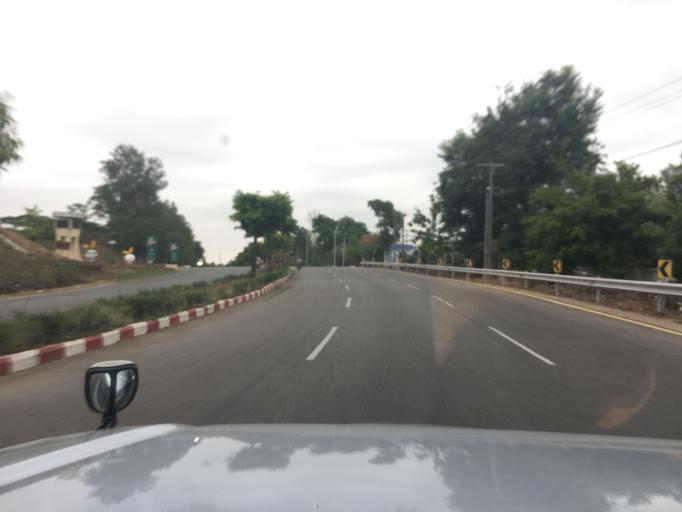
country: MM
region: Bago
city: Thanatpin
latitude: 17.2172
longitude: 96.4301
